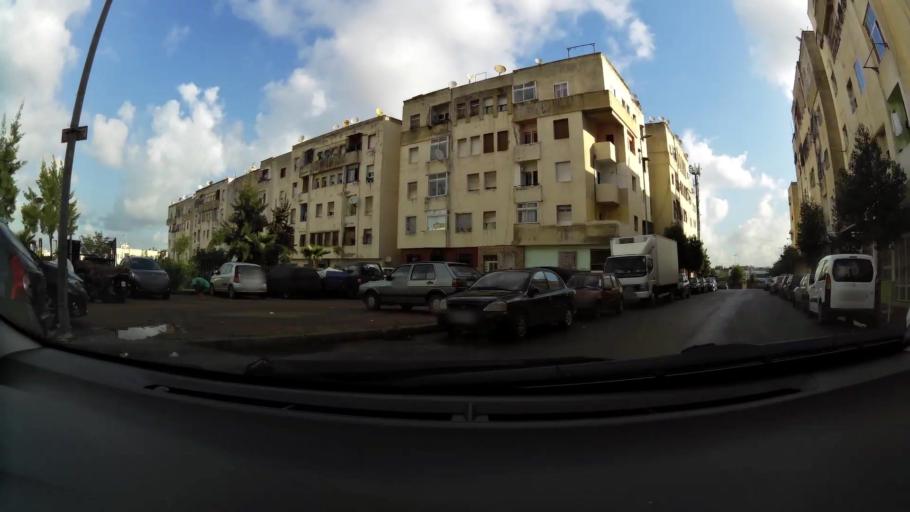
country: MA
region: Grand Casablanca
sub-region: Mediouna
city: Tit Mellil
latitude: 33.5950
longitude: -7.5338
